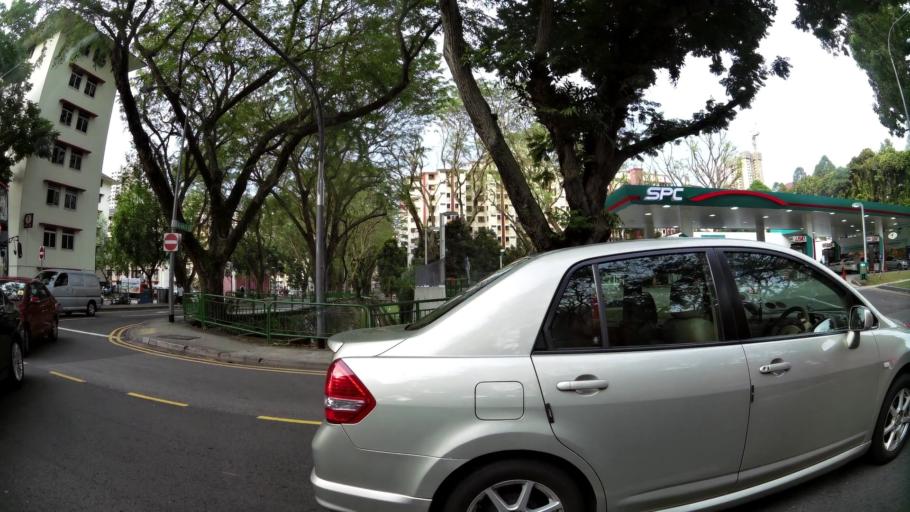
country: SG
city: Singapore
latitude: 1.2840
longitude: 103.8182
